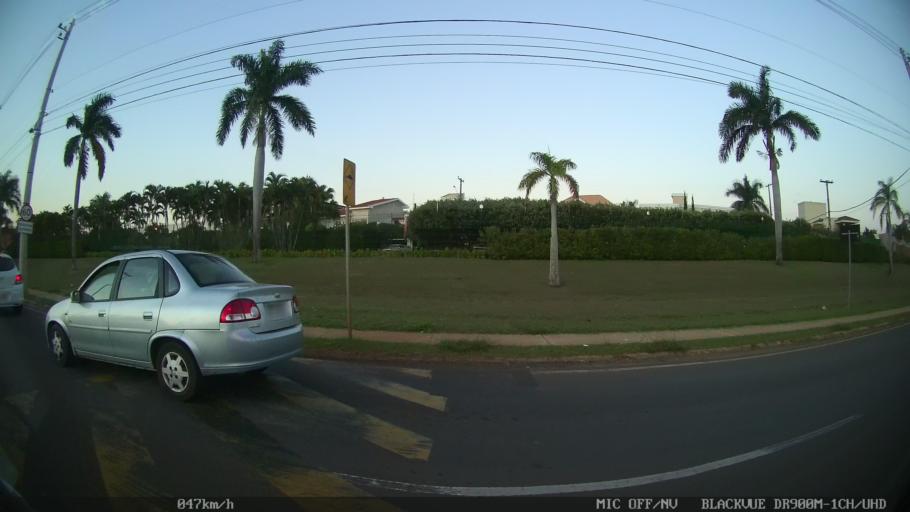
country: BR
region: Sao Paulo
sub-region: Sao Jose Do Rio Preto
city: Sao Jose do Rio Preto
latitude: -20.8144
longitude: -49.3476
